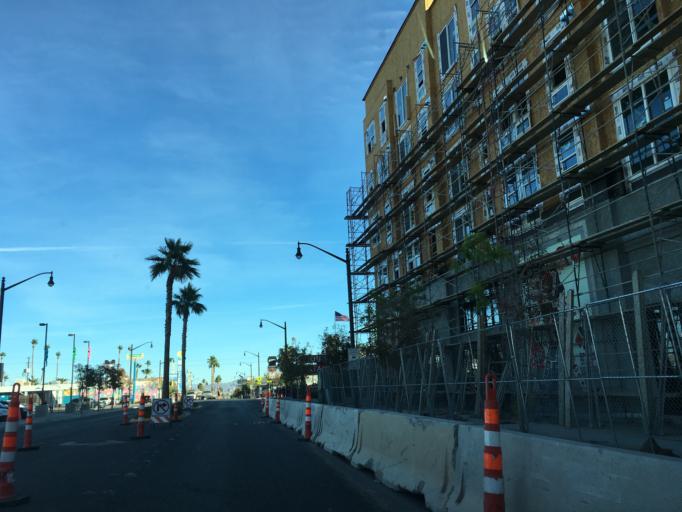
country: US
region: Nevada
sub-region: Clark County
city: Las Vegas
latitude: 36.1672
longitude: -115.1360
